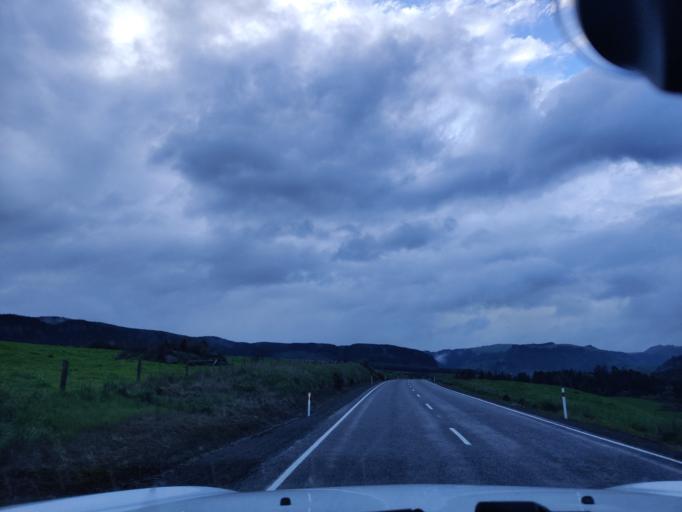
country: NZ
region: Waikato
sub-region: South Waikato District
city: Tokoroa
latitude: -38.4124
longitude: 175.8041
